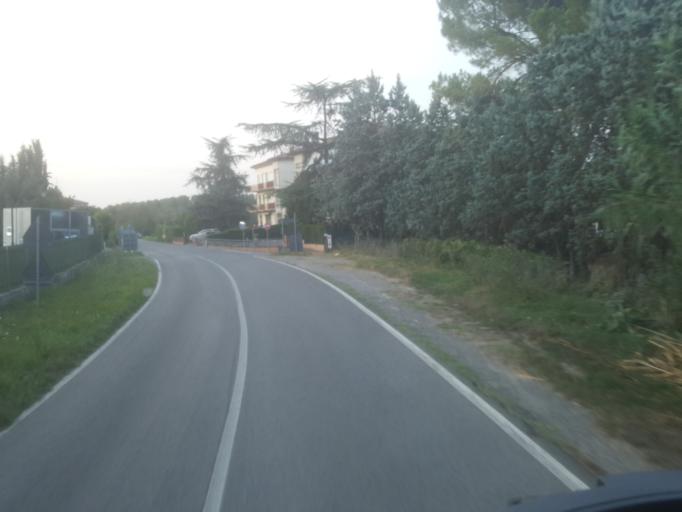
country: IT
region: Tuscany
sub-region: Province of Florence
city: Certaldo
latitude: 43.5353
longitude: 11.0345
